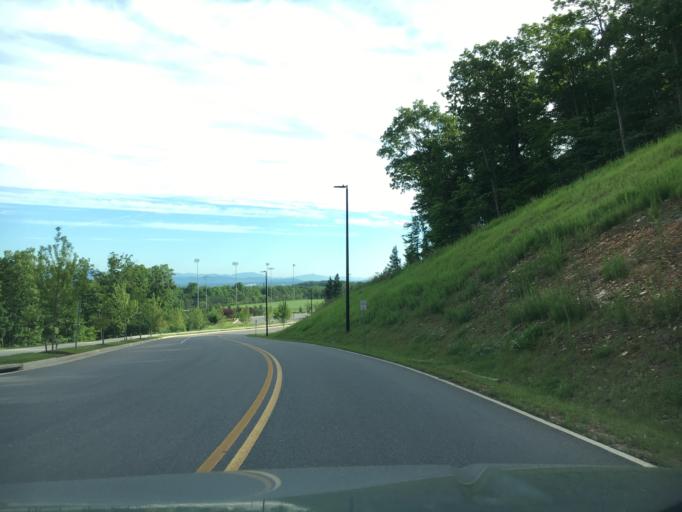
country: US
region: Virginia
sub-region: City of Lynchburg
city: West Lynchburg
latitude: 37.3547
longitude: -79.1673
